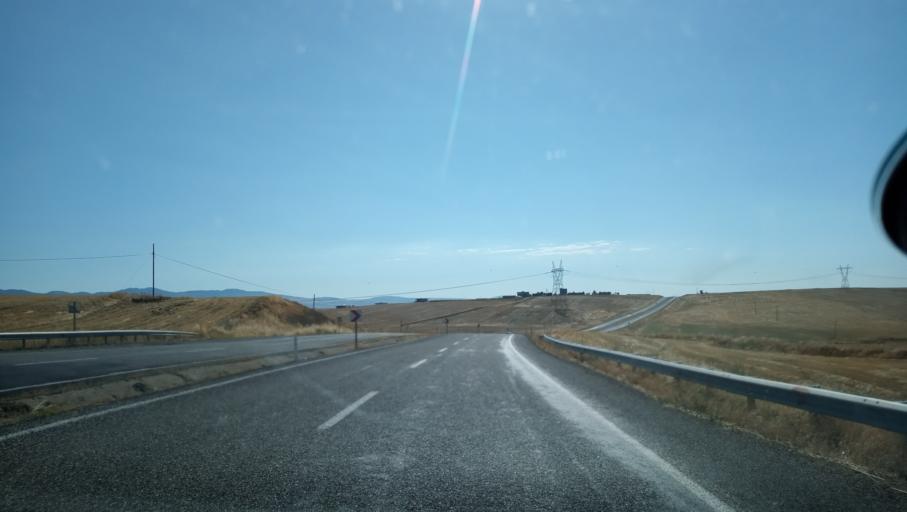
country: TR
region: Diyarbakir
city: Bagdere
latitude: 38.1309
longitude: 40.7630
